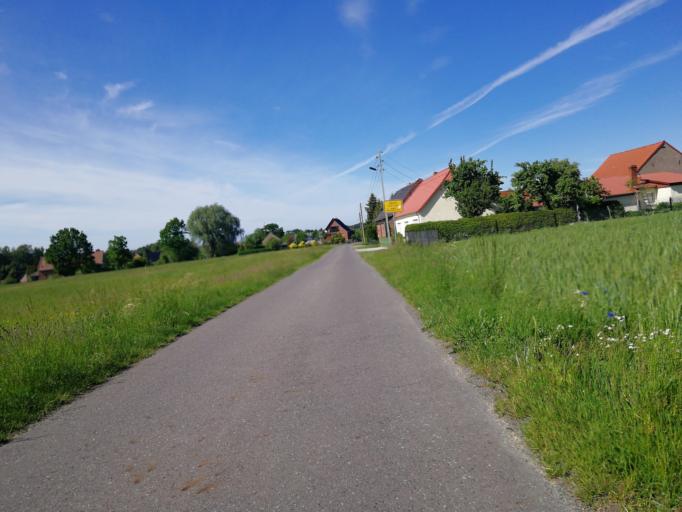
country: DE
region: Brandenburg
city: Calau
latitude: 51.7423
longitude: 13.9198
